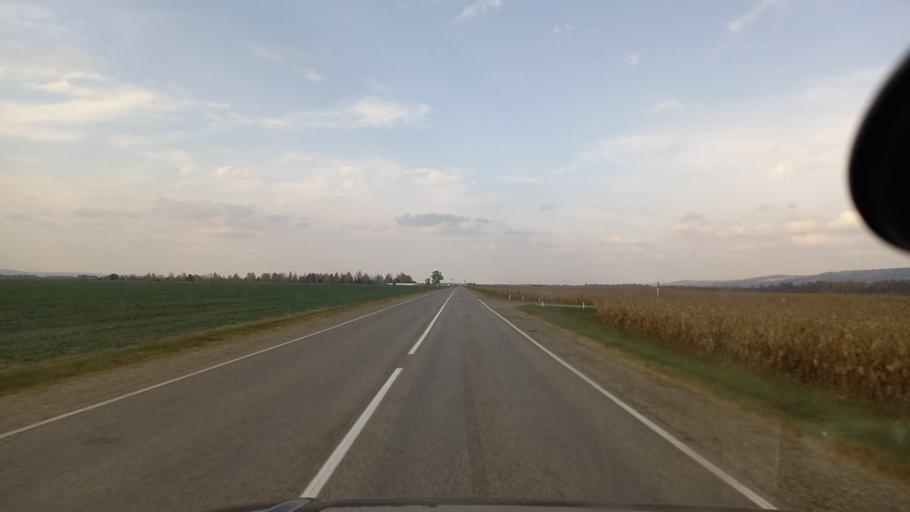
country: RU
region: Krasnodarskiy
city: Perepravnaya
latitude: 44.3417
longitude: 40.8436
